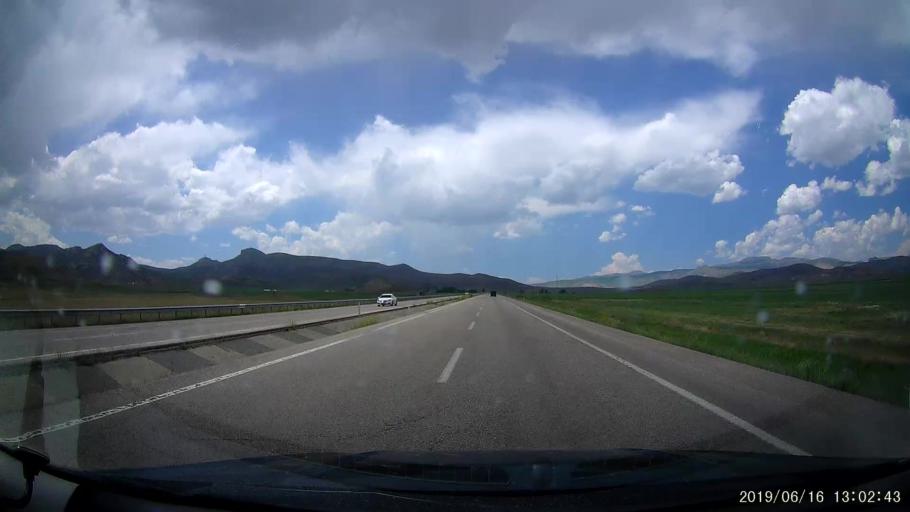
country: TR
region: Agri
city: Sulucem
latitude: 39.5763
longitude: 43.8087
